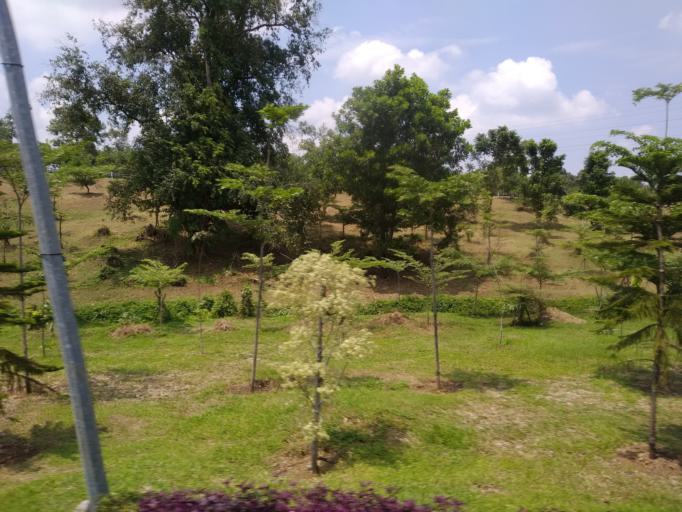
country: ID
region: West Java
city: Bogor
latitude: -6.5954
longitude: 106.8336
